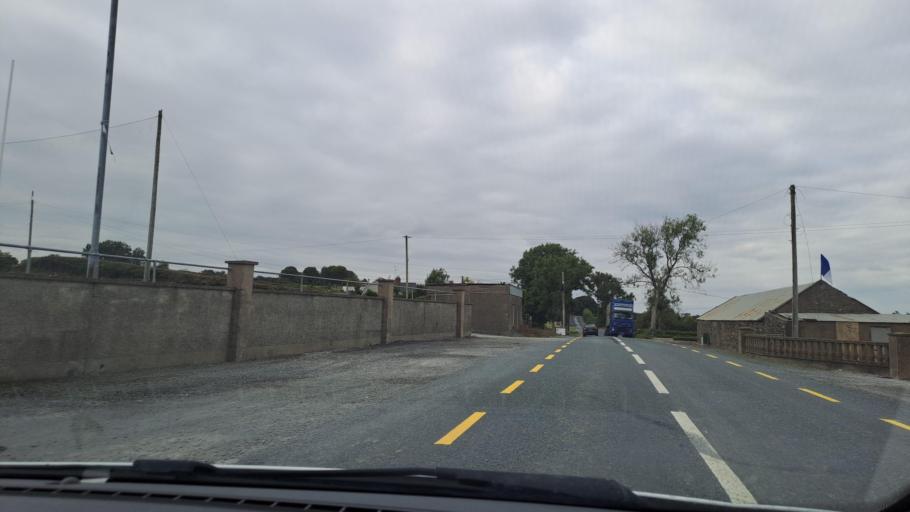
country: IE
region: Ulster
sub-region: An Cabhan
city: Kingscourt
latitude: 53.9806
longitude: -6.8796
